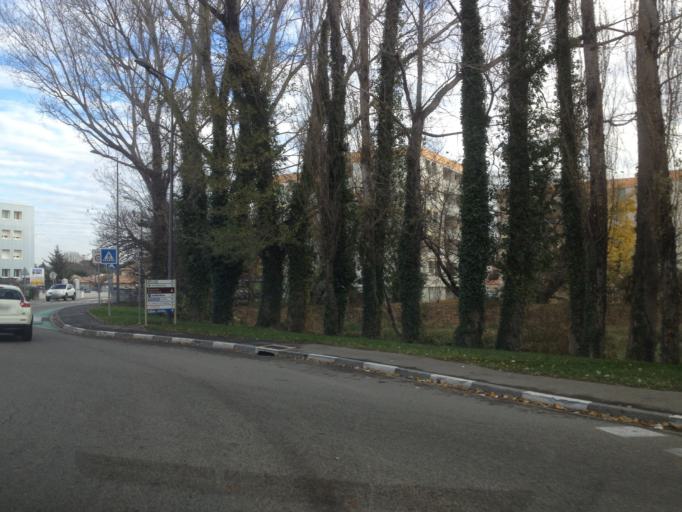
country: FR
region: Provence-Alpes-Cote d'Azur
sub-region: Departement du Vaucluse
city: Sorgues
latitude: 44.0022
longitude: 4.8777
